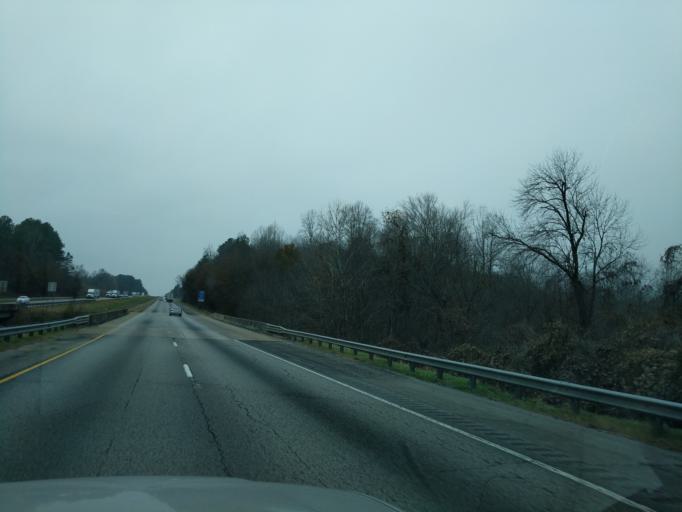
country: US
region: Georgia
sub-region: Franklin County
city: Carnesville
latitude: 34.3397
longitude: -83.3348
